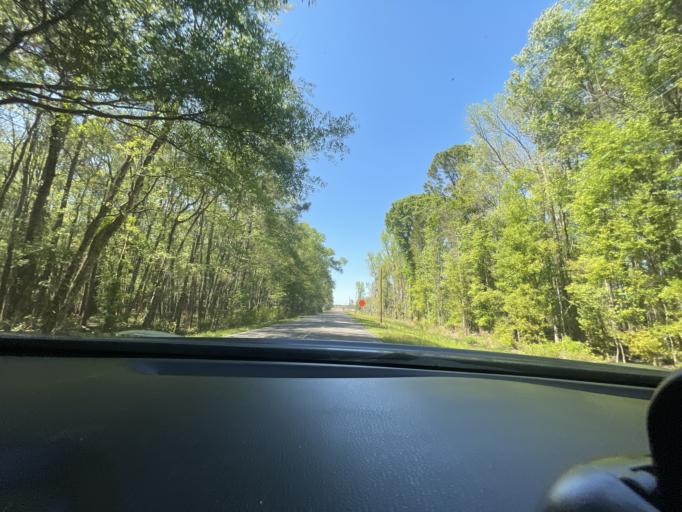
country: US
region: Georgia
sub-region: Chatham County
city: Bloomingdale
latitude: 32.1126
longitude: -81.3132
